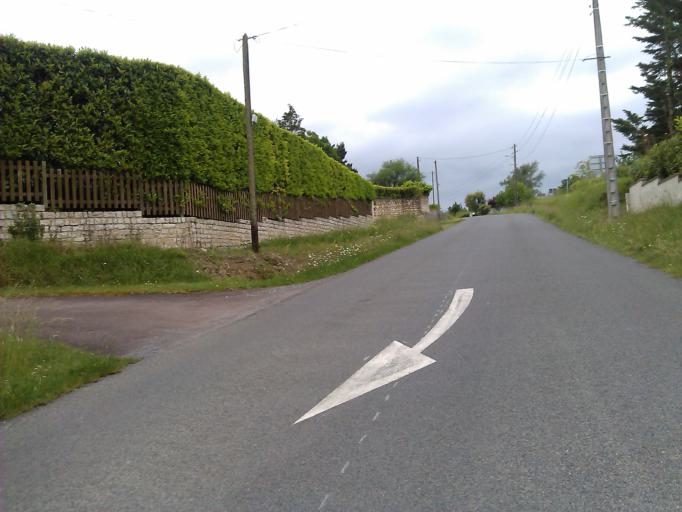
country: FR
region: Poitou-Charentes
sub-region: Departement de la Charente
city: Chateauneuf-sur-Charente
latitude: 45.5886
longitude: -0.0529
